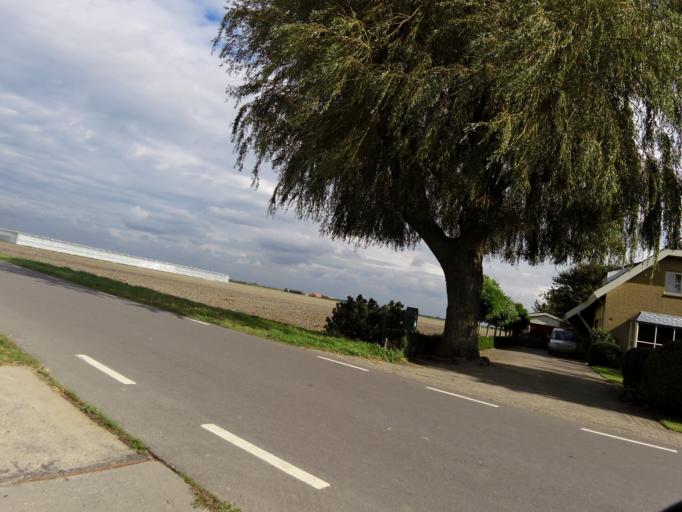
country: NL
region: South Holland
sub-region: Gemeente Rijnwoude
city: Benthuizen
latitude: 52.0514
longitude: 4.5751
